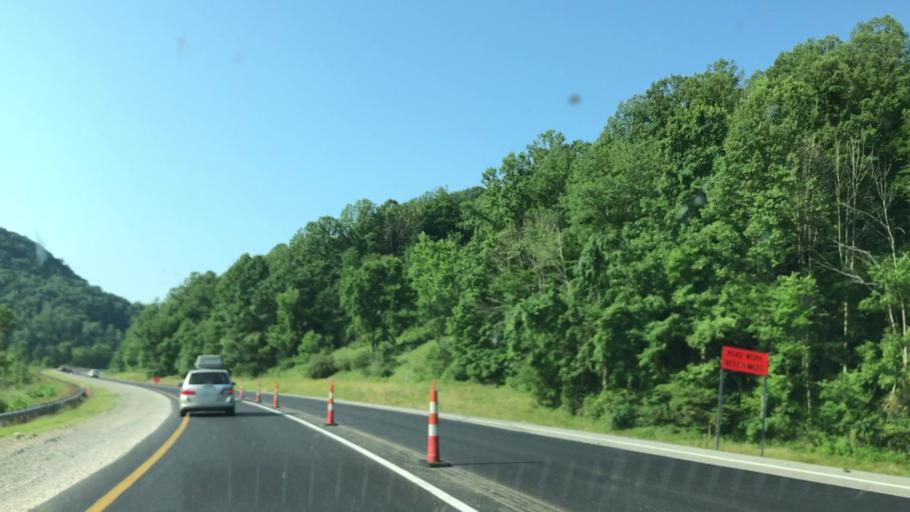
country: US
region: West Virginia
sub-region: Braxton County
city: Sutton
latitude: 38.7497
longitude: -80.6777
